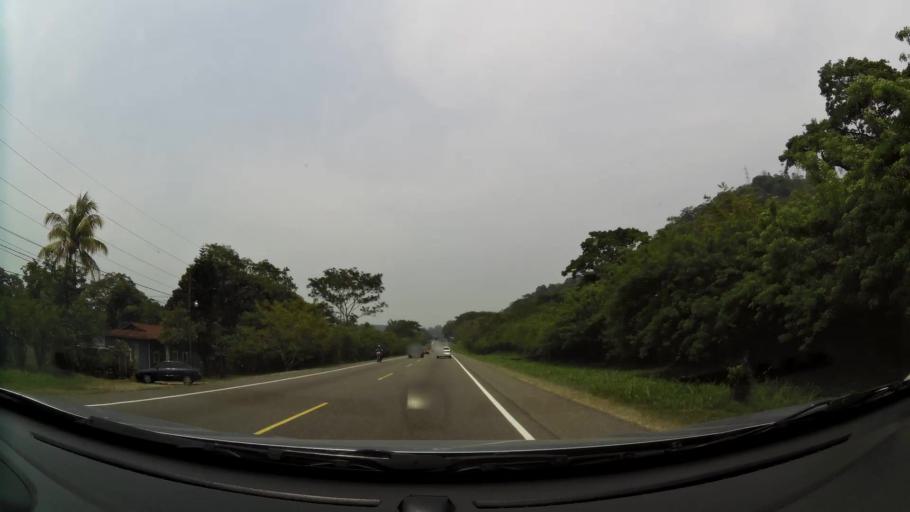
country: HN
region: Cortes
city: La Guama
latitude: 14.8753
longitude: -87.9446
